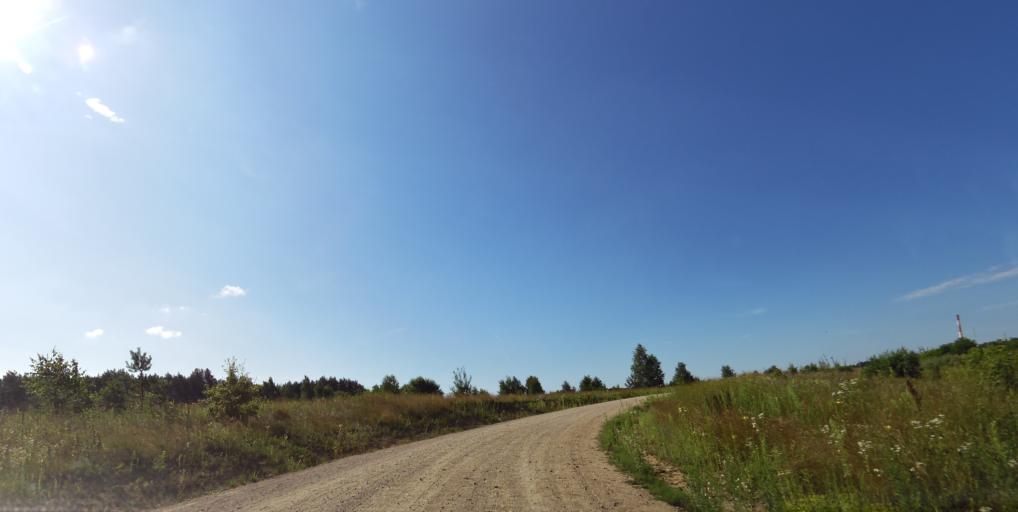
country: LT
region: Vilnius County
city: Pilaite
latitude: 54.6916
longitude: 25.1795
